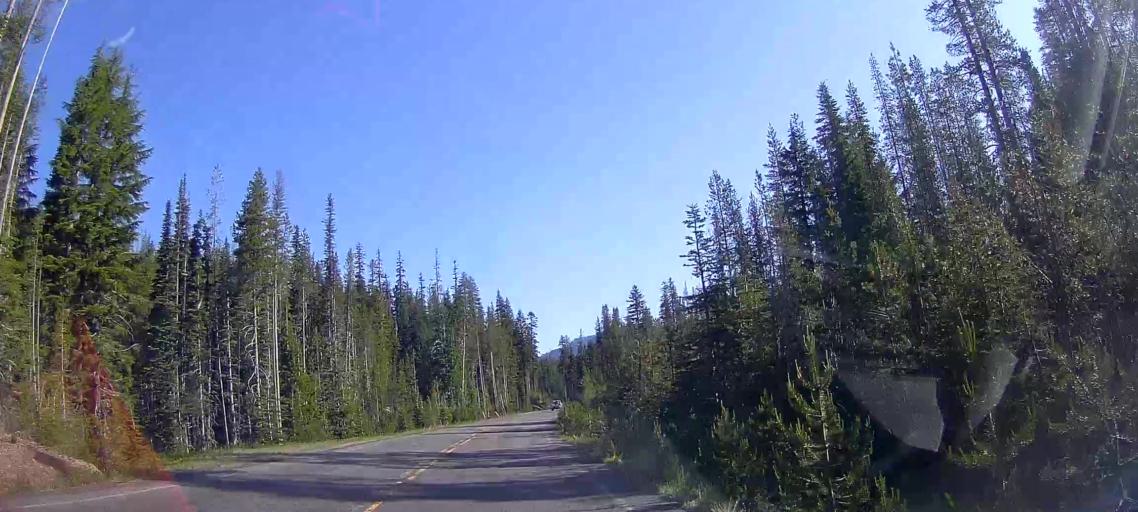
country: US
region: Oregon
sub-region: Jackson County
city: Shady Cove
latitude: 42.8436
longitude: -122.1471
